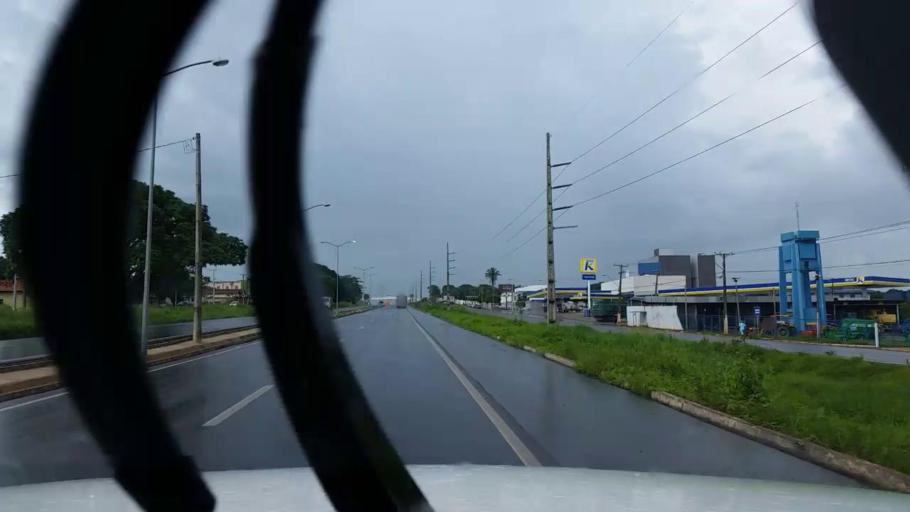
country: BR
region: Tocantins
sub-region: Araguaina
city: Araguaina
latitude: -7.2041
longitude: -48.2399
